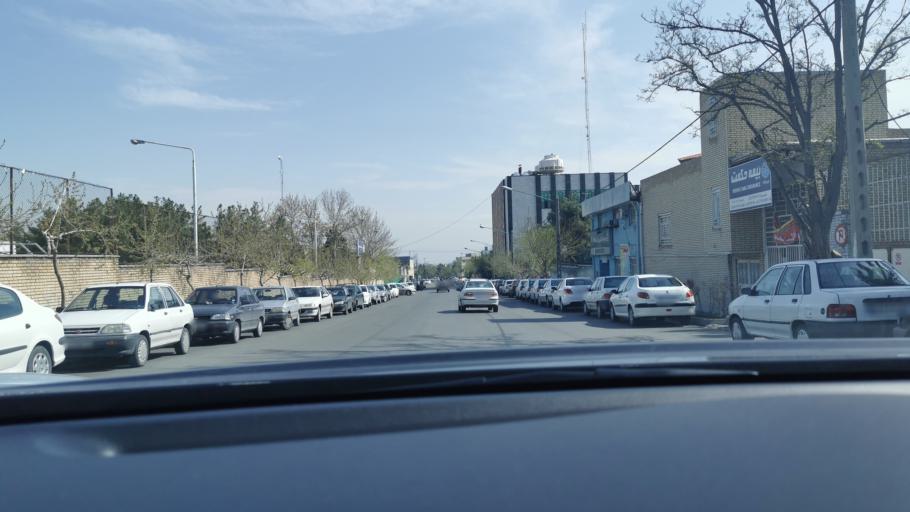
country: IR
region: Razavi Khorasan
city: Mashhad
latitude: 36.2809
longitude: 59.5498
